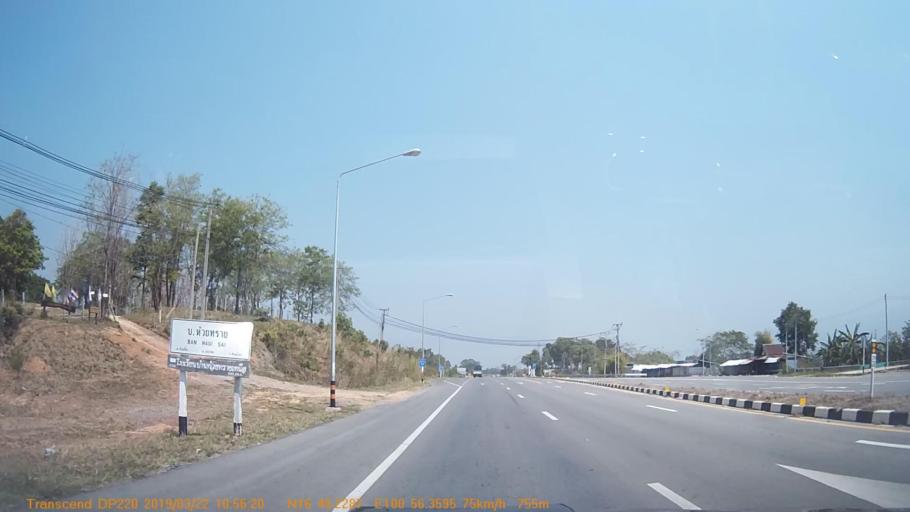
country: TH
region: Phetchabun
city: Khao Kho
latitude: 16.8209
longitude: 100.9393
